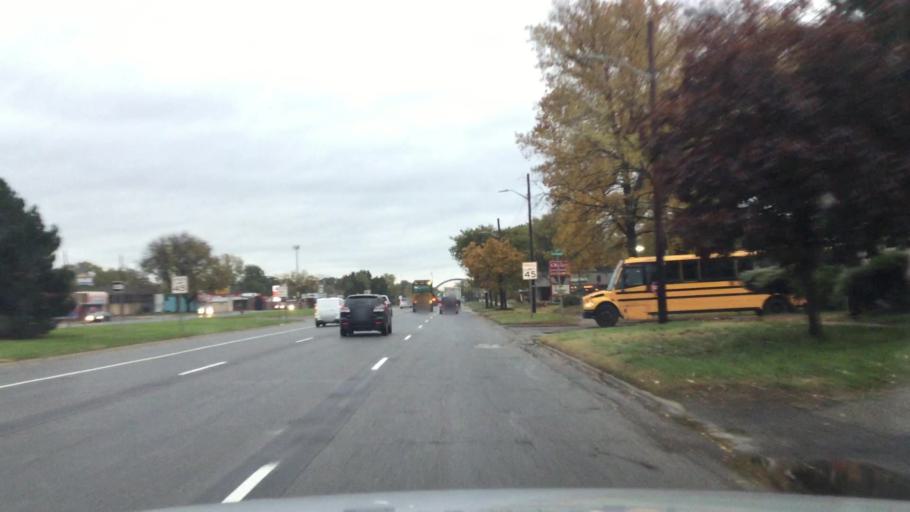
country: US
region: Michigan
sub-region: Wayne County
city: Taylor
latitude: 42.2756
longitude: -83.2709
